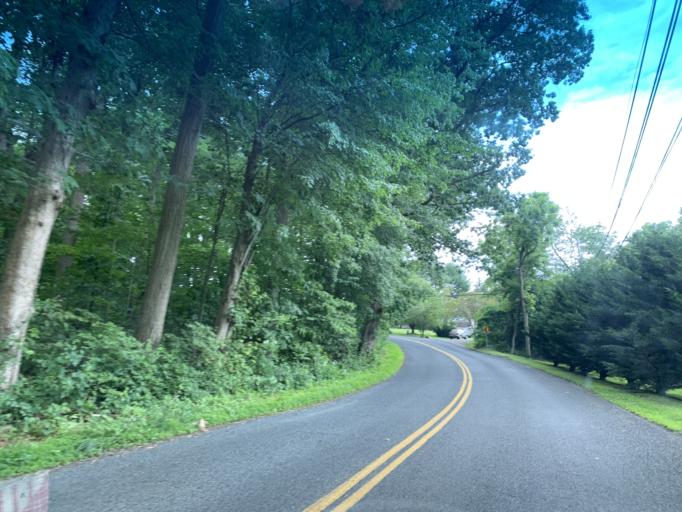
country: US
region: Maryland
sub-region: Harford County
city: Fallston
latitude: 39.5376
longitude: -76.4376
